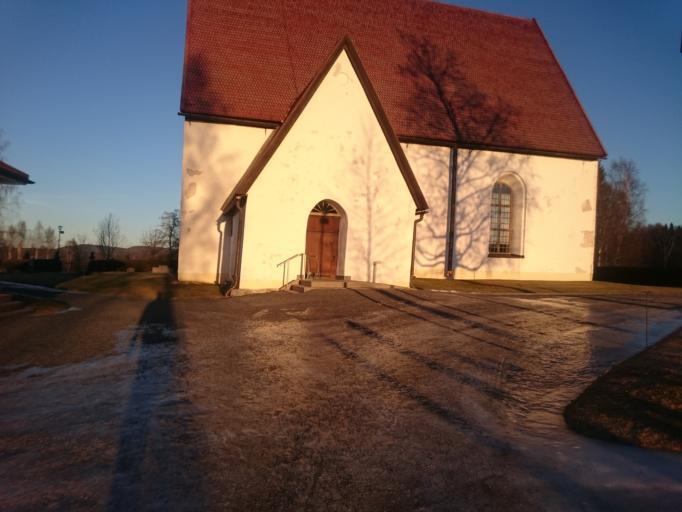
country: SE
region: Vaesternorrland
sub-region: OErnskoeldsviks Kommun
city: Bjasta
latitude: 63.2908
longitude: 18.2948
